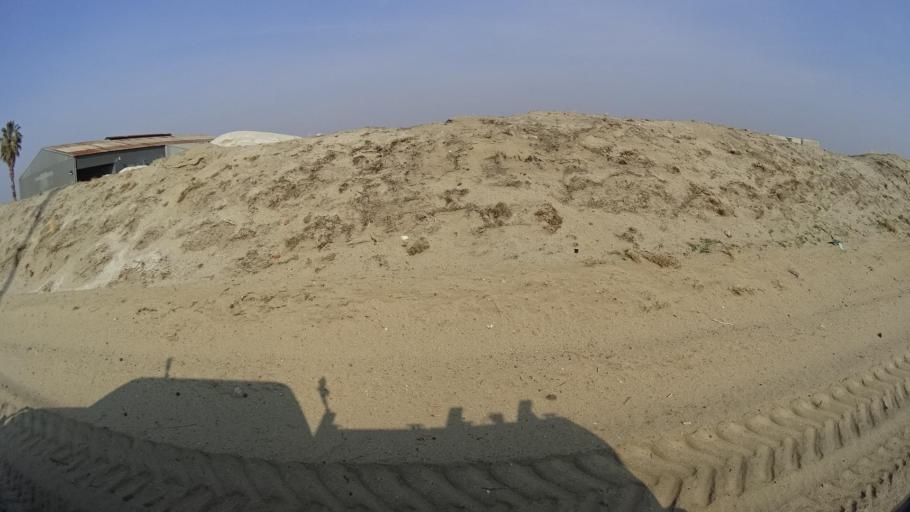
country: US
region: California
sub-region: Kern County
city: Arvin
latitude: 35.0930
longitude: -118.9104
